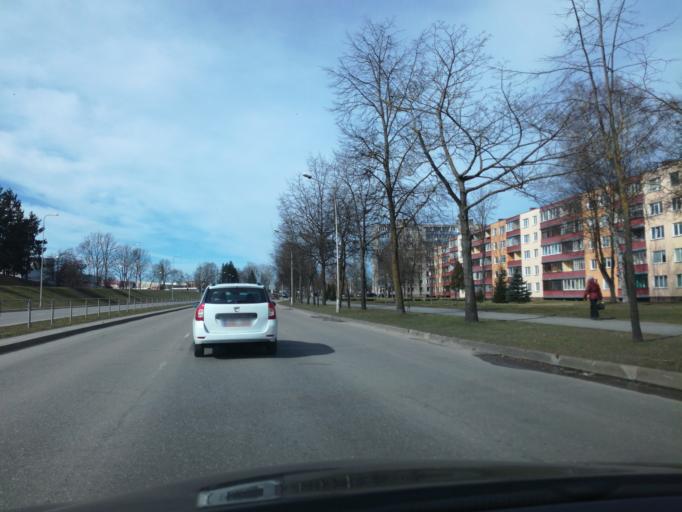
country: LT
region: Alytaus apskritis
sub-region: Alytus
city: Alytus
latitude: 54.3984
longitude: 24.0263
